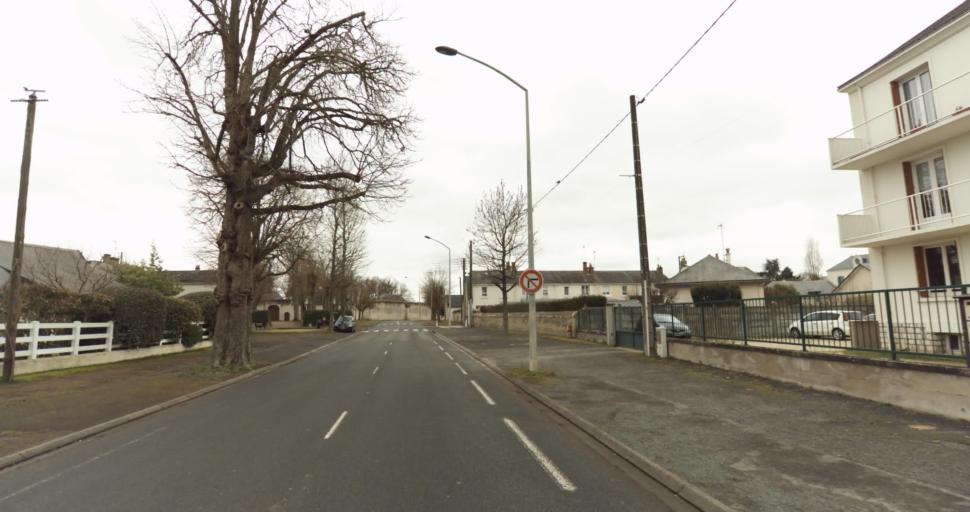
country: FR
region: Pays de la Loire
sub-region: Departement de Maine-et-Loire
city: Saumur
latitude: 47.2434
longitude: -0.0897
